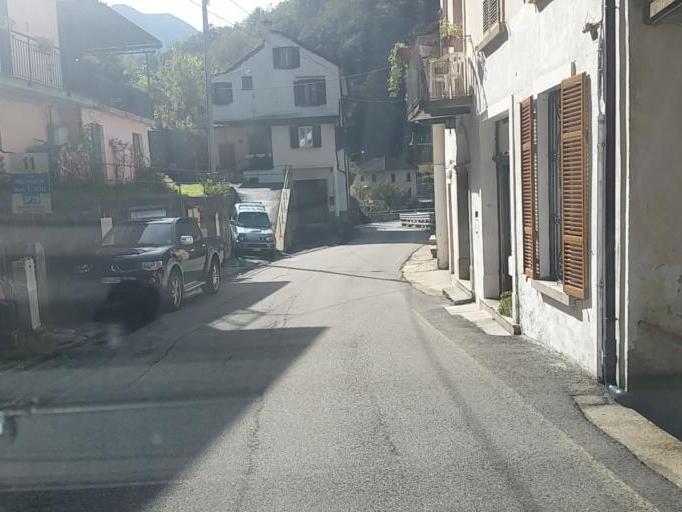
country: IT
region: Piedmont
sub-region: Provincia Verbano-Cusio-Ossola
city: Falmenta
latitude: 46.0869
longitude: 8.5998
